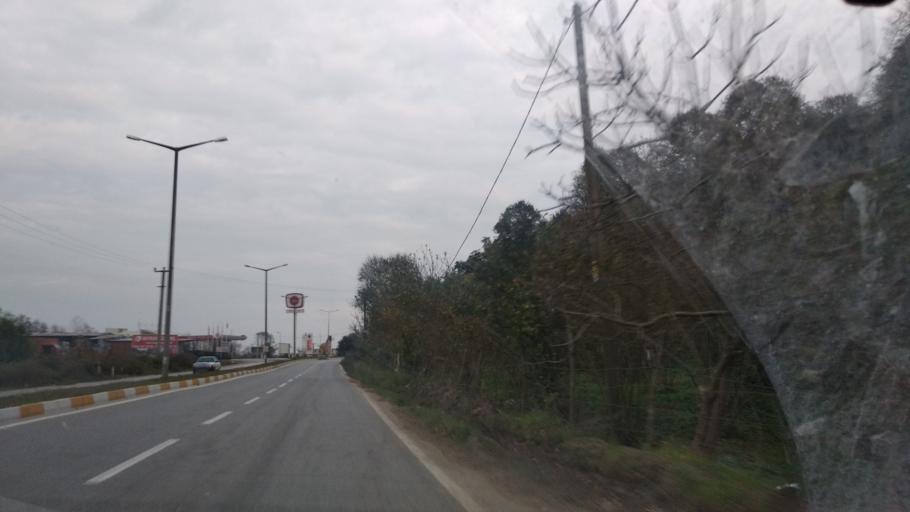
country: TR
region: Sakarya
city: Karasu
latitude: 41.1000
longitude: 30.6668
